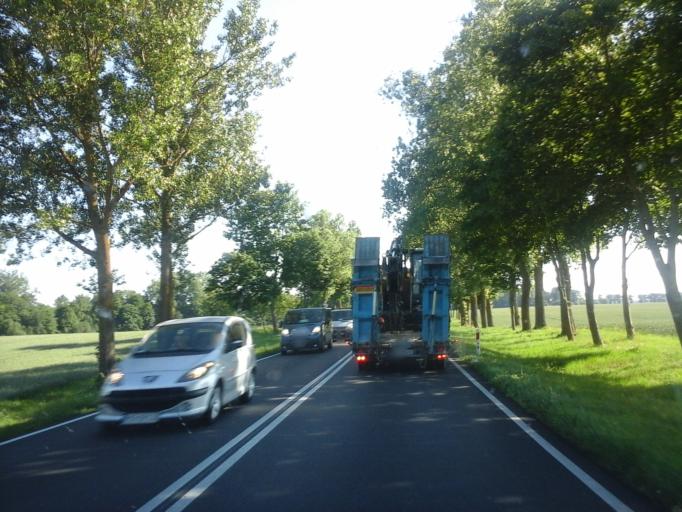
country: PL
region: West Pomeranian Voivodeship
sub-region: Powiat gryficki
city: Ploty
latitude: 53.7821
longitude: 15.2487
